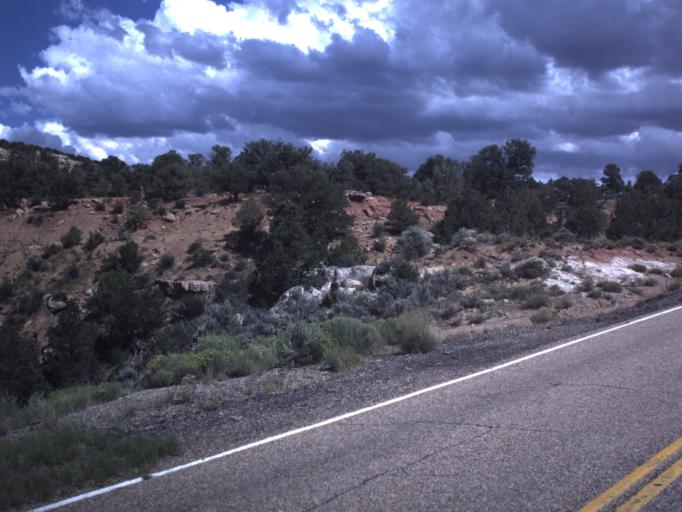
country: US
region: Utah
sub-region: Duchesne County
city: Duchesne
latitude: 40.3128
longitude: -110.7001
